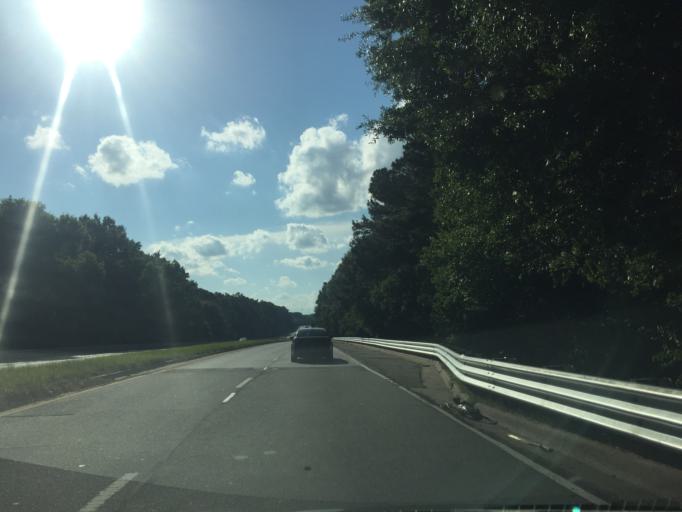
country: US
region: Georgia
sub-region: Chatham County
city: Savannah
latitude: 32.0356
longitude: -81.1348
